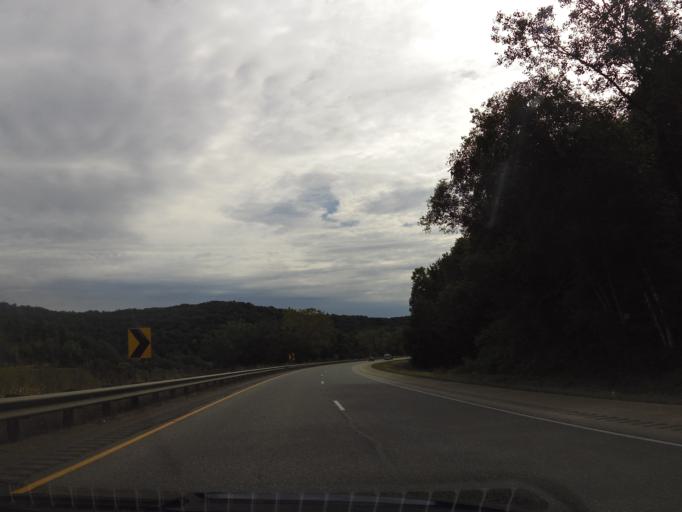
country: US
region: Wisconsin
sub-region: Trempealeau County
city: Trempealeau
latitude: 43.9324
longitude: -91.4199
